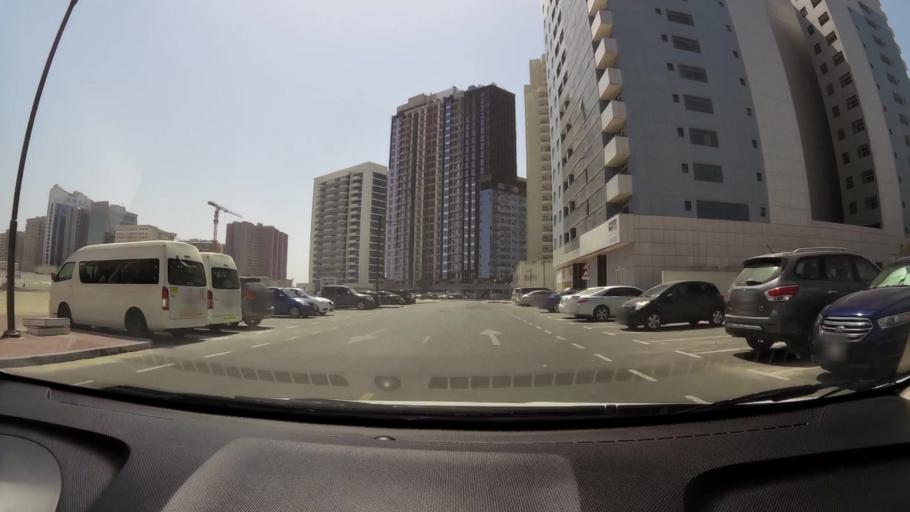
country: AE
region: Ash Shariqah
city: Sharjah
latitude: 25.2878
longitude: 55.3639
